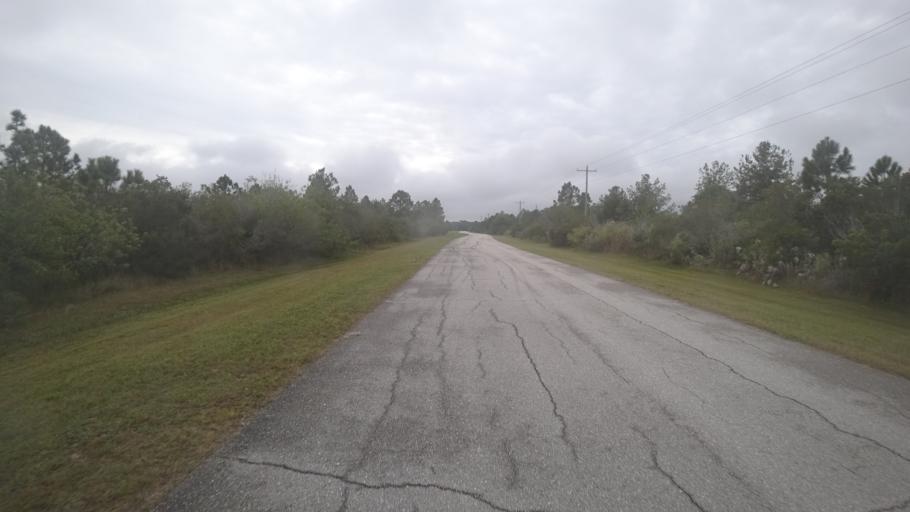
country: US
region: Florida
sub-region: Sarasota County
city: The Meadows
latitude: 27.4052
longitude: -82.3402
